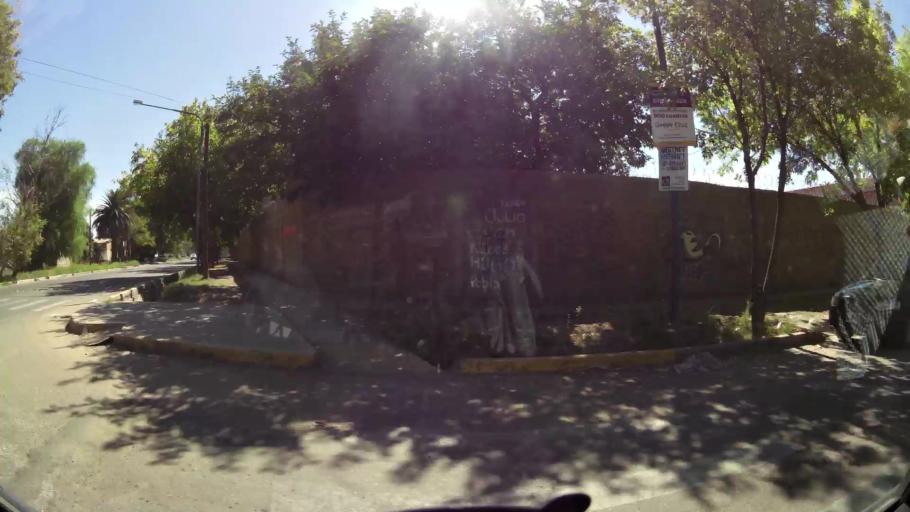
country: AR
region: Mendoza
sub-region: Departamento de Godoy Cruz
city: Godoy Cruz
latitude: -32.9537
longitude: -68.8230
